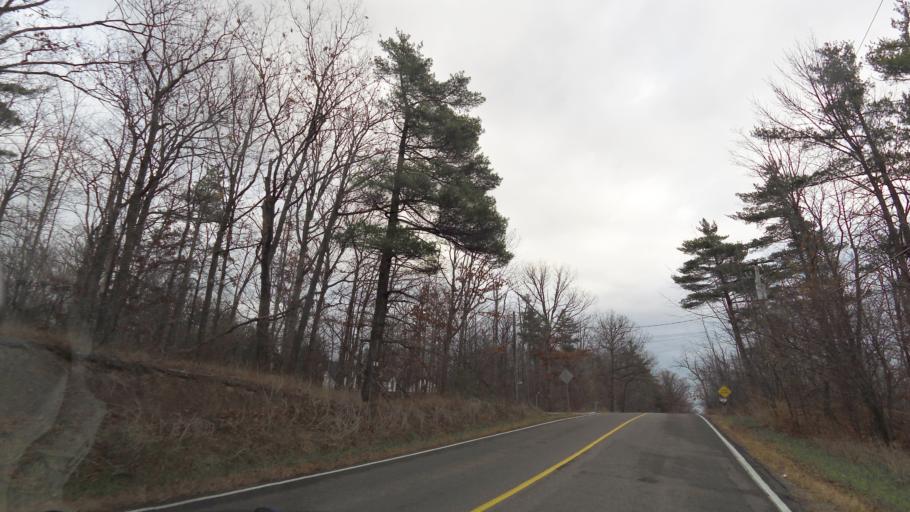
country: CA
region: Ontario
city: Burlington
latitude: 43.4042
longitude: -79.8403
